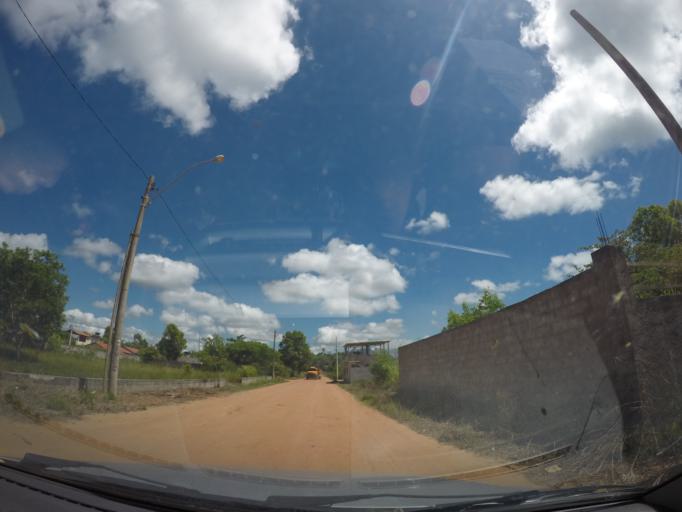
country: BR
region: Espirito Santo
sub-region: Serra
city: Serra
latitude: -20.0123
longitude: -40.1575
